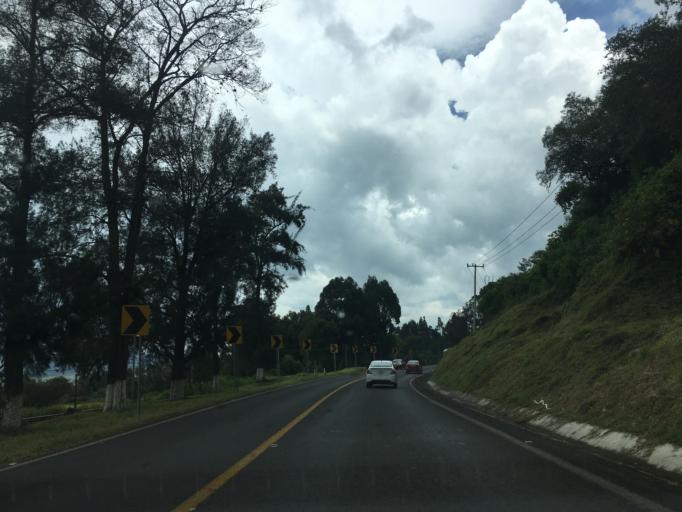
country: MX
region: Michoacan
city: Patzcuaro
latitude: 19.5438
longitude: -101.6071
